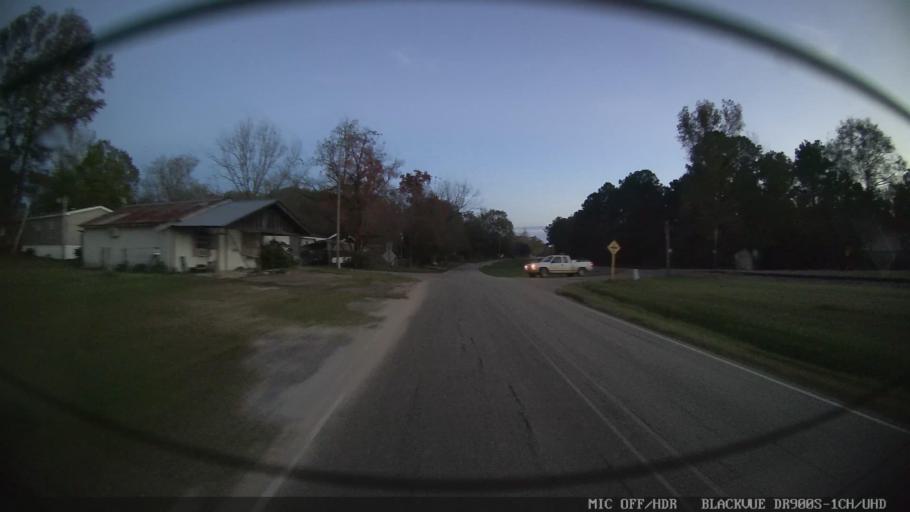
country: US
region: Mississippi
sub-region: Forrest County
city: Hattiesburg
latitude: 31.1659
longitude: -89.2147
